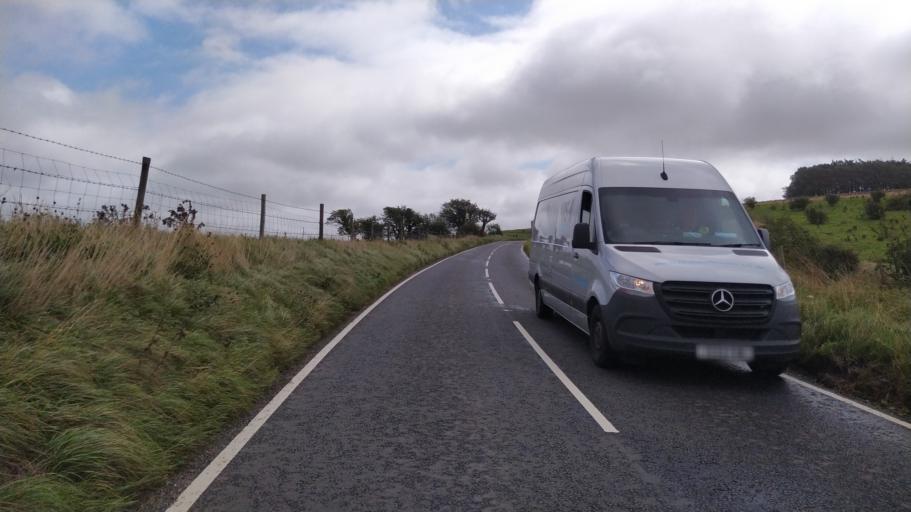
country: GB
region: England
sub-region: Dorset
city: Shaftesbury
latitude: 50.9872
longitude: -2.1510
